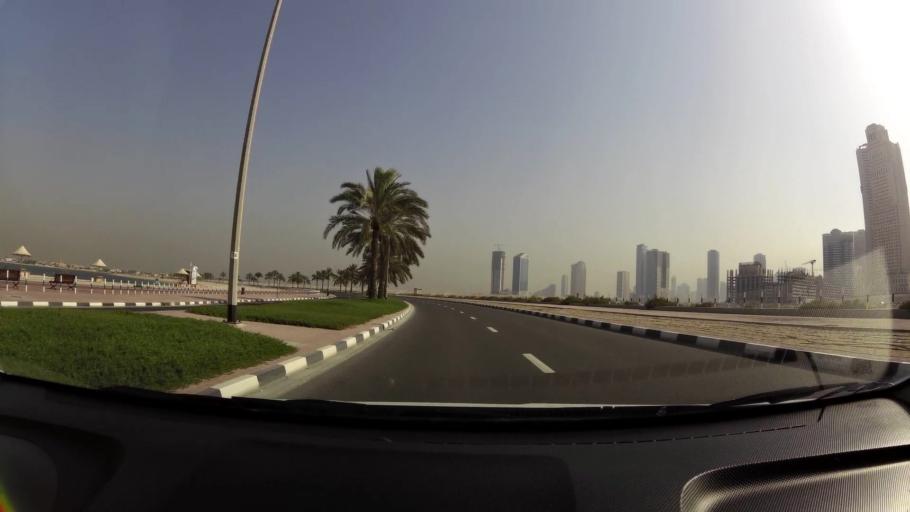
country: AE
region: Ash Shariqah
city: Sharjah
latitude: 25.3015
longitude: 55.3585
